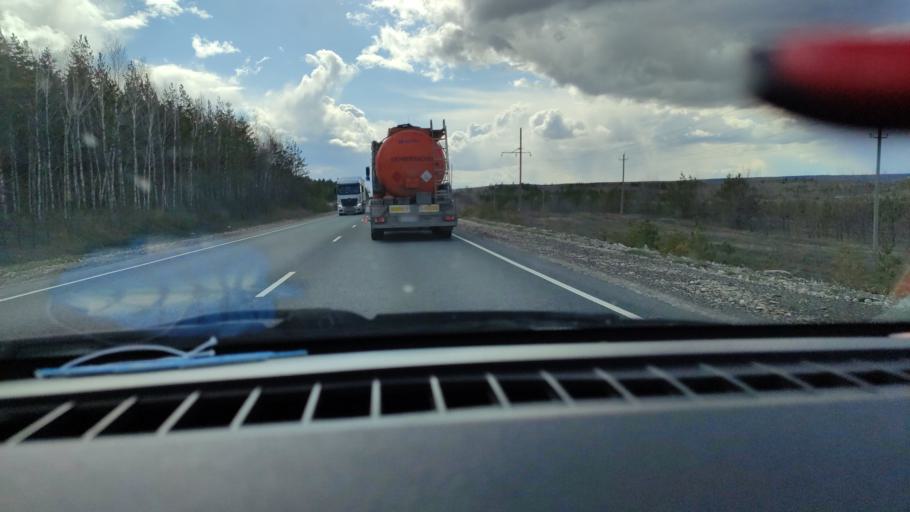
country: RU
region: Saratov
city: Khvalynsk
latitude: 52.5374
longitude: 48.0463
